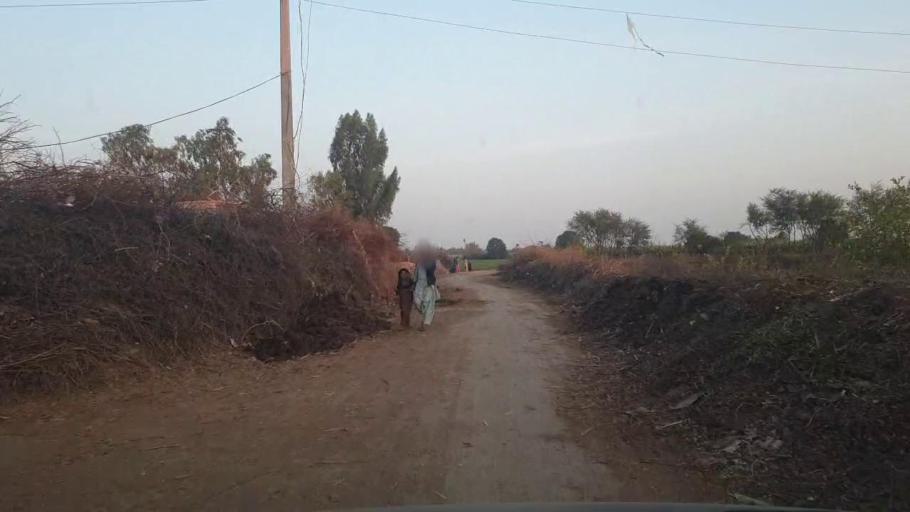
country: PK
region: Sindh
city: Bhit Shah
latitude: 25.8696
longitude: 68.5358
